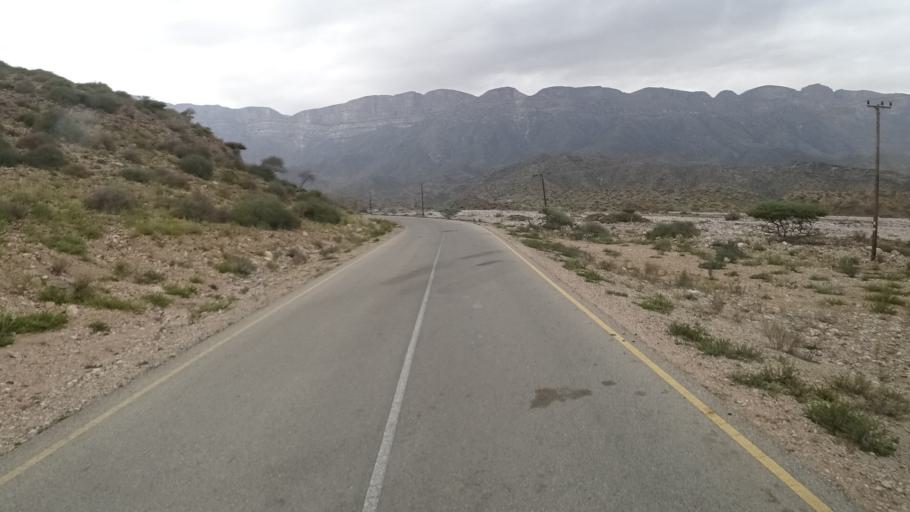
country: OM
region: Zufar
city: Salalah
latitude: 17.1699
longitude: 54.9738
